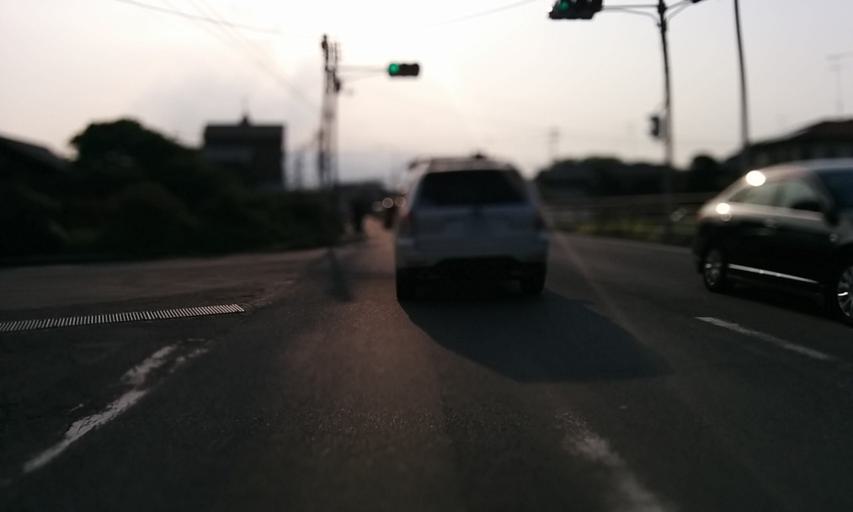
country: JP
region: Ehime
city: Saijo
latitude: 33.8968
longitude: 133.1200
